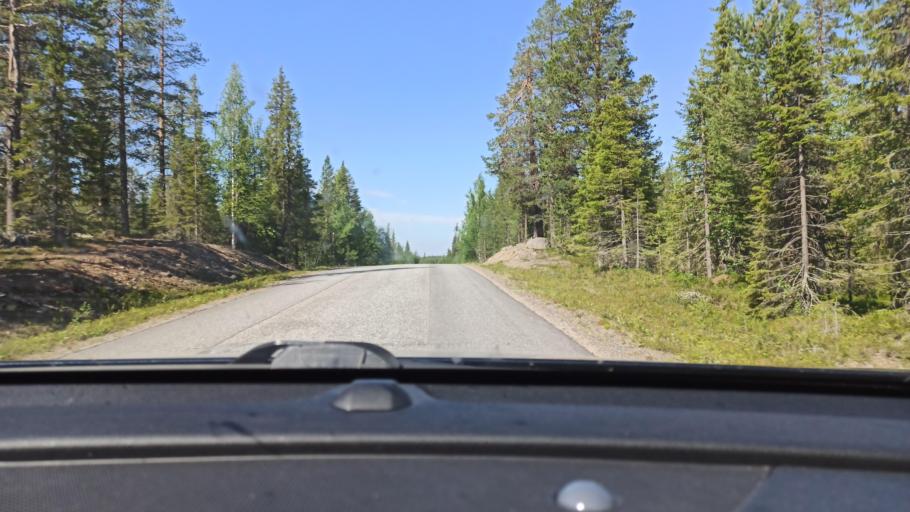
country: FI
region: Lapland
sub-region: Tunturi-Lappi
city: Kolari
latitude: 67.6830
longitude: 24.1307
